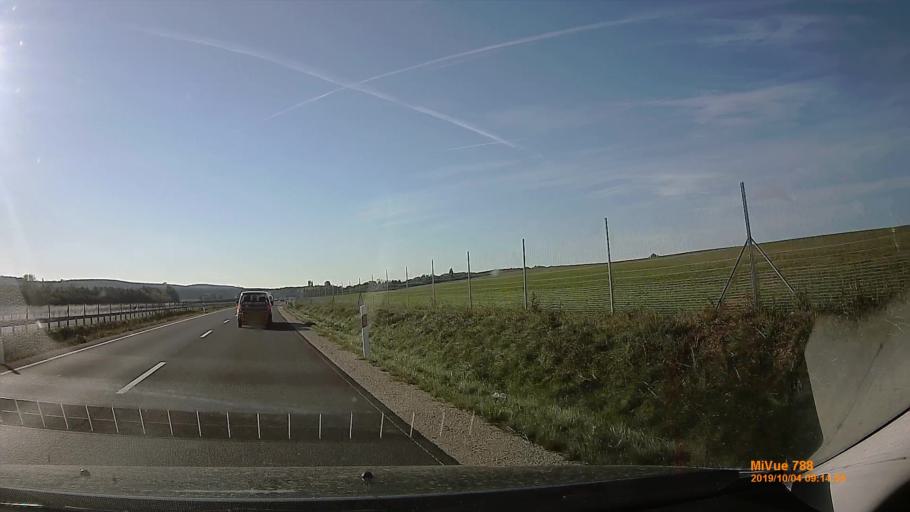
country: HU
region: Somogy
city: Karad
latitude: 46.6307
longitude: 17.7916
